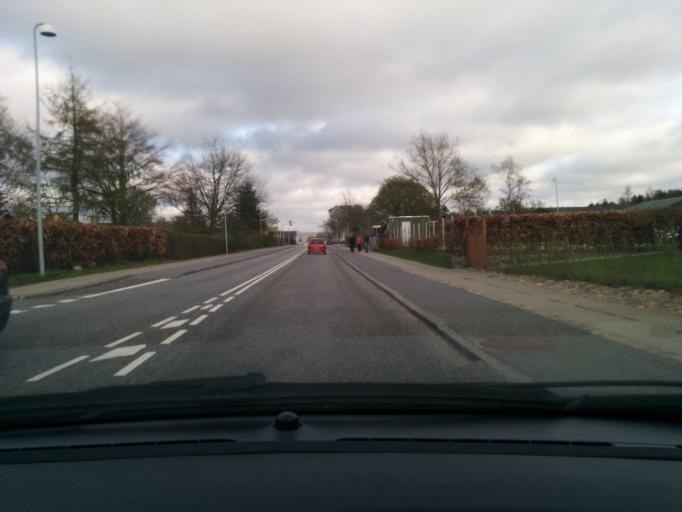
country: DK
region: Central Jutland
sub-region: Favrskov Kommune
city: Hadsten
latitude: 56.3217
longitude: 10.0367
